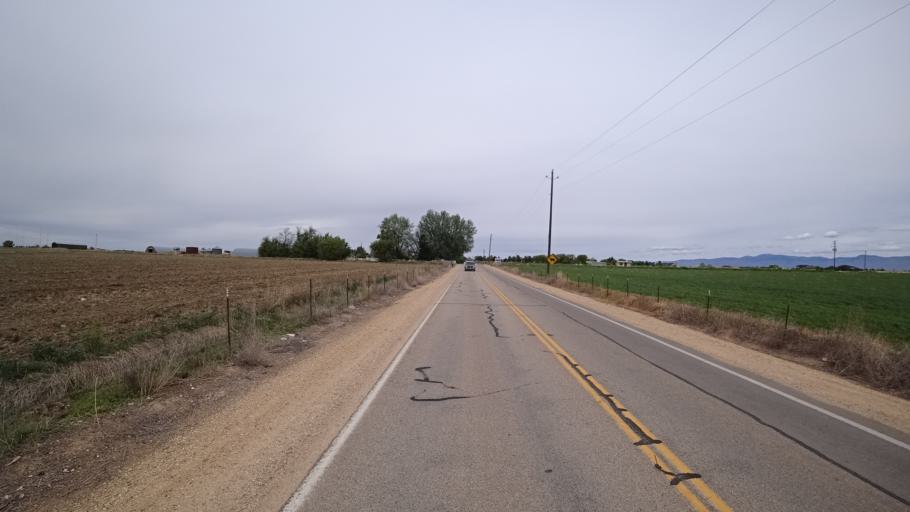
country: US
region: Idaho
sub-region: Ada County
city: Meridian
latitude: 43.5489
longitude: -116.3747
